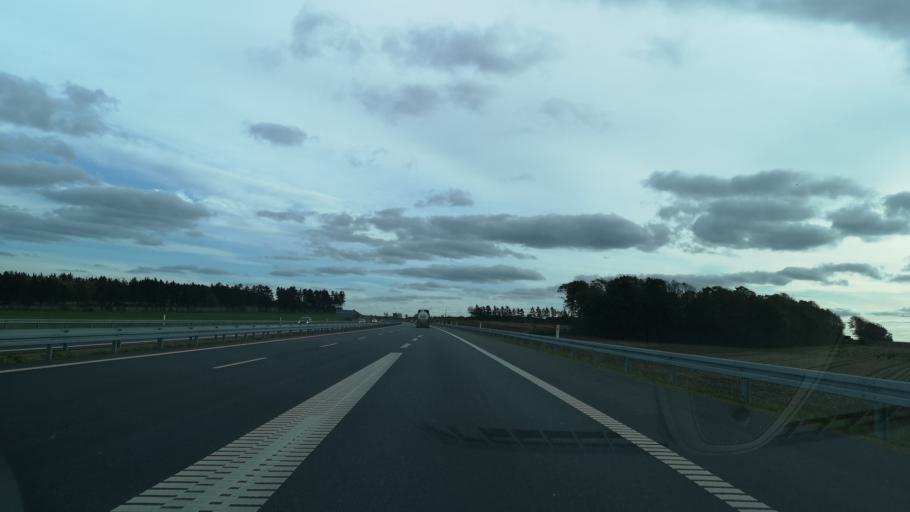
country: DK
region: Central Jutland
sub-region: Herning Kommune
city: Avlum
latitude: 56.2893
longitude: 8.7308
